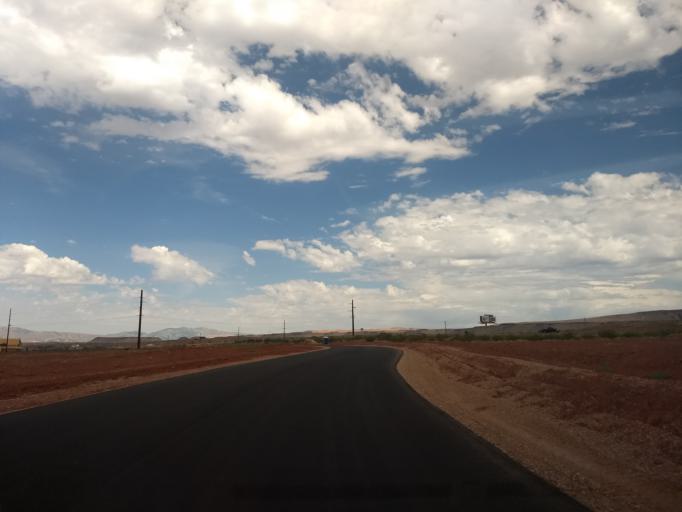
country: US
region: Utah
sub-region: Washington County
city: Washington
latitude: 37.1433
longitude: -113.4920
